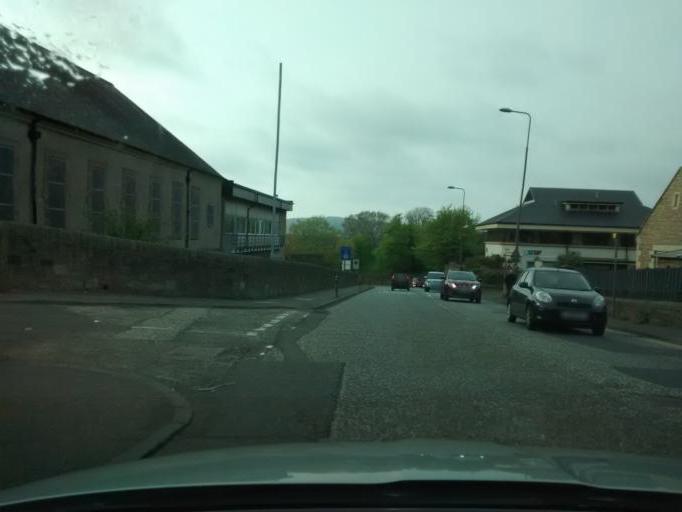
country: GB
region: Scotland
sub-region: Edinburgh
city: Colinton
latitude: 55.9232
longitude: -3.2445
